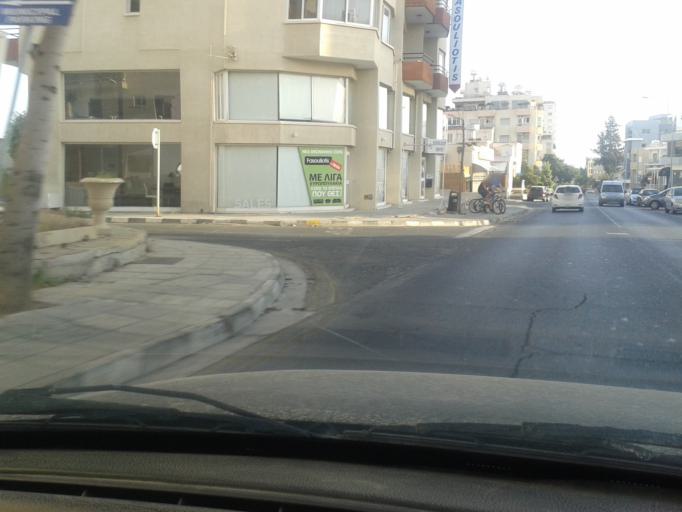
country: CY
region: Limassol
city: Limassol
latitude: 34.6923
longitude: 33.0449
